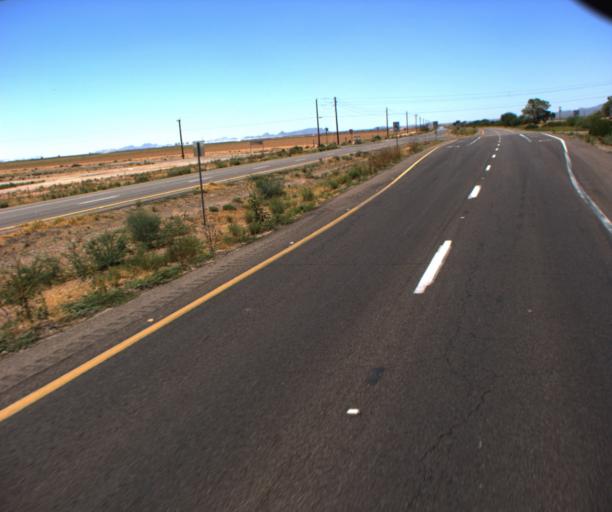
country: US
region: Arizona
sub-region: Pinal County
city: Maricopa
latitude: 32.9409
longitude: -112.0491
